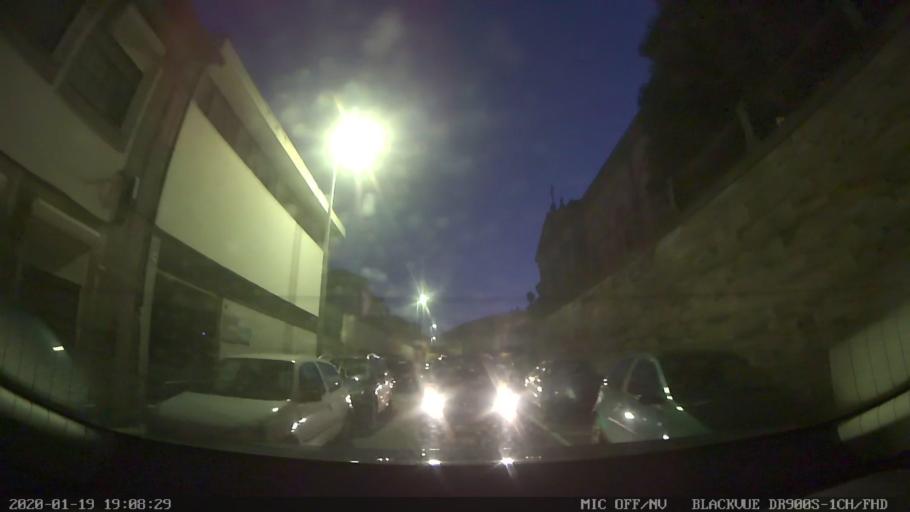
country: PT
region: Porto
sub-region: Porto
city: Porto
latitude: 41.1505
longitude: -8.6279
